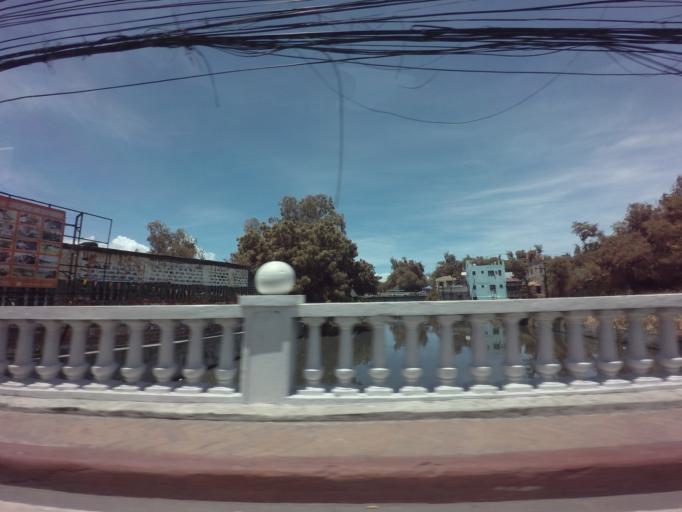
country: PH
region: Calabarzon
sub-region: Province of Rizal
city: Las Pinas
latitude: 14.4748
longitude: 120.9783
